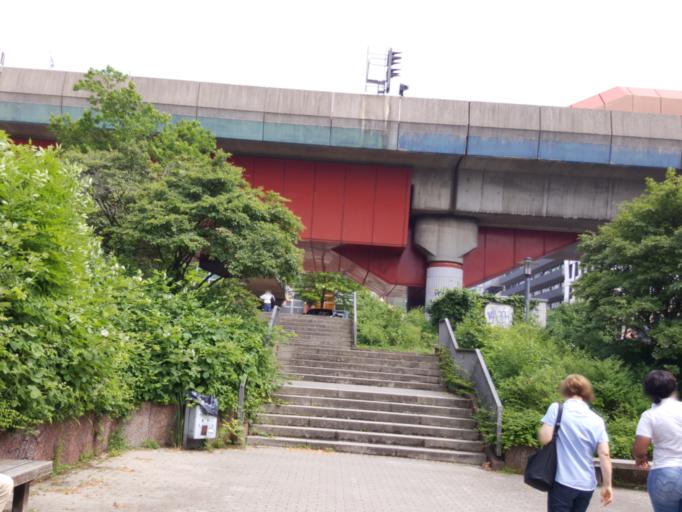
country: DE
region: Hamburg
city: Hamburg-Mitte
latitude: 53.5473
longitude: 10.0226
